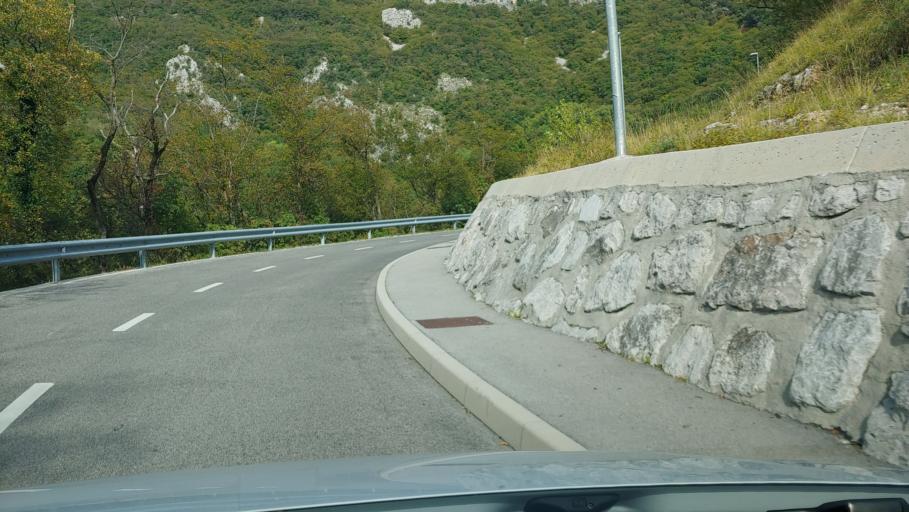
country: SI
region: Ajdovscina
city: Ajdovscina
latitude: 45.9016
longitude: 13.9079
